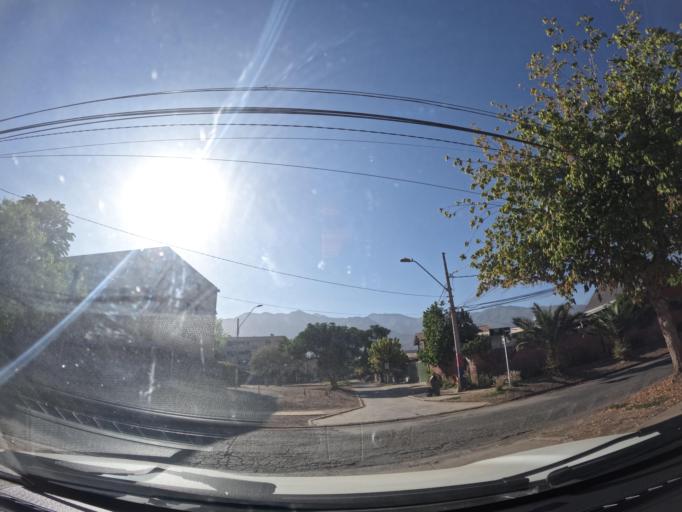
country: CL
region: Santiago Metropolitan
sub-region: Provincia de Santiago
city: Villa Presidente Frei, Nunoa, Santiago, Chile
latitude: -33.4638
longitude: -70.5537
